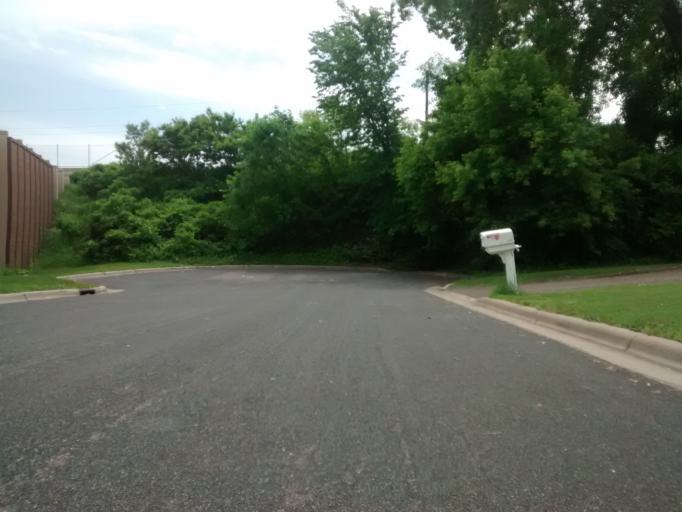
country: US
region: Minnesota
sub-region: Dakota County
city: Burnsville
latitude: 44.7527
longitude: -93.2871
